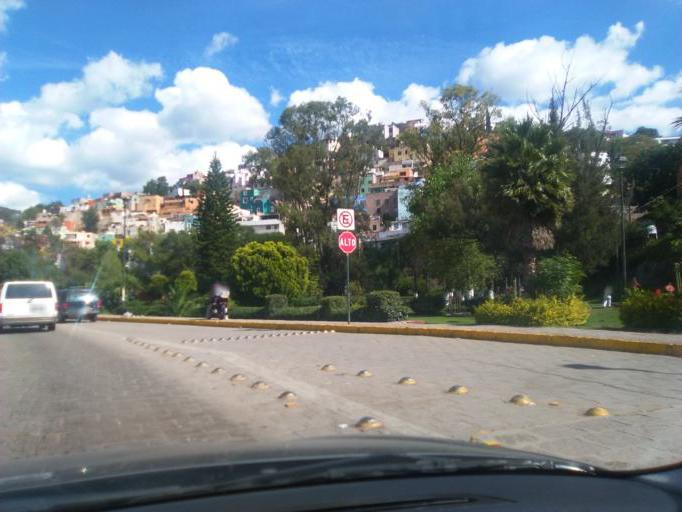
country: MX
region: Guanajuato
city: Guanajuato
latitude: 21.0158
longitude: -101.2655
